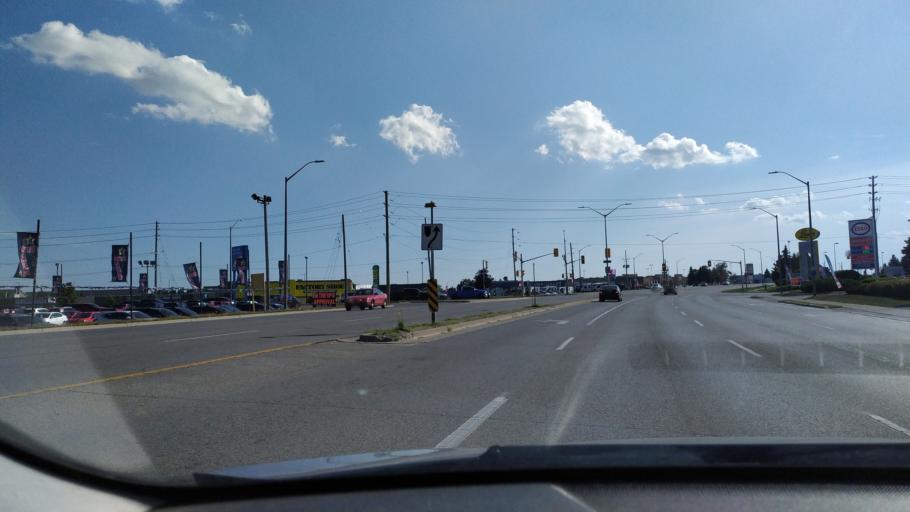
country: CA
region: Ontario
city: London
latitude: 42.9417
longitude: -81.2577
